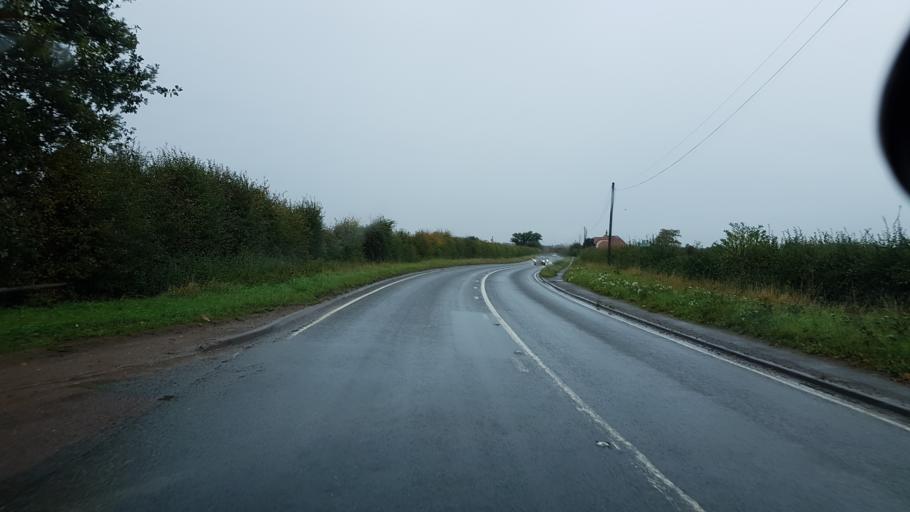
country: GB
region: England
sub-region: Worcestershire
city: Upton upon Severn
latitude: 52.0571
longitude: -2.1926
